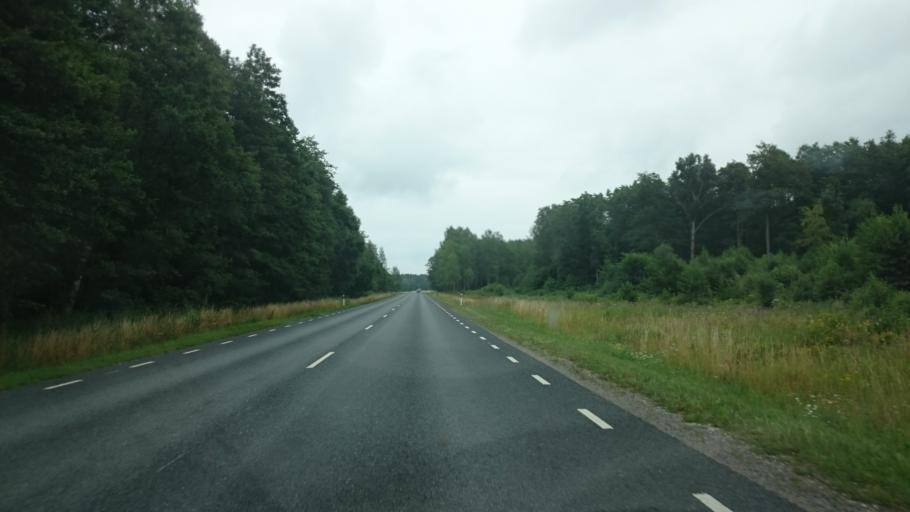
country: EE
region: Saare
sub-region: Orissaare vald
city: Orissaare
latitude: 58.6035
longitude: 23.3054
